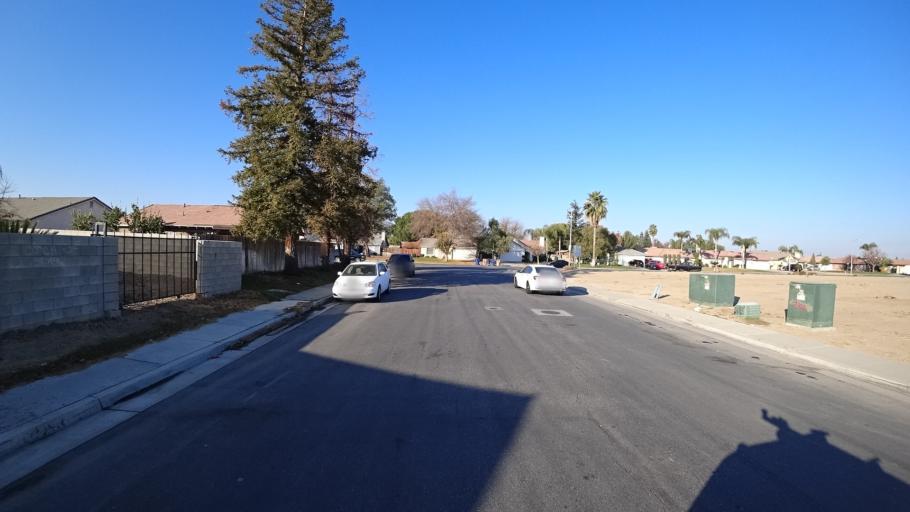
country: US
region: California
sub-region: Kern County
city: Greenfield
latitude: 35.2981
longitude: -119.0074
